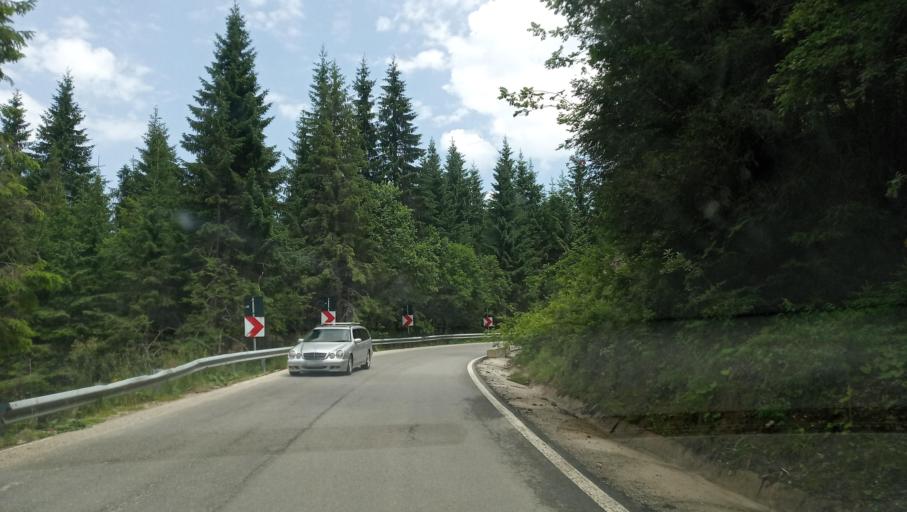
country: RO
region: Dambovita
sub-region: Comuna Moroeni
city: Glod
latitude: 45.3276
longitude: 25.4355
